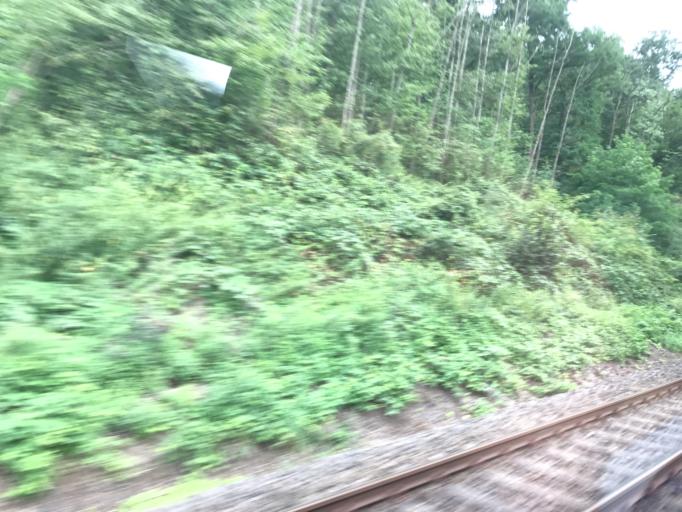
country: DE
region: Hesse
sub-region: Regierungsbezirk Giessen
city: Steeden
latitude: 50.3972
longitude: 8.1223
